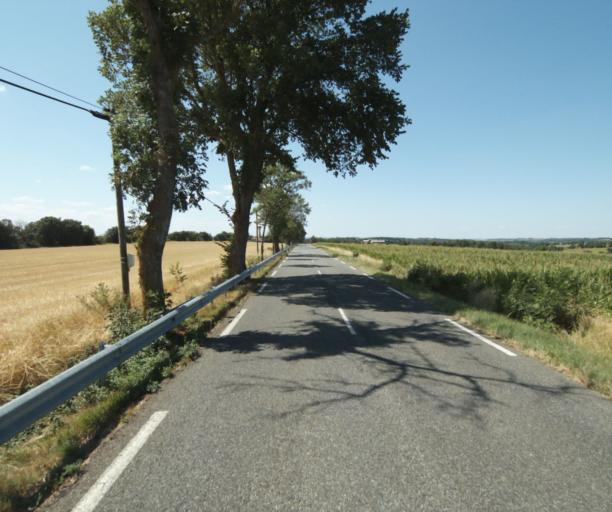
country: FR
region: Midi-Pyrenees
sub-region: Departement de la Haute-Garonne
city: Saint-Felix-Lauragais
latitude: 43.5022
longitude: 1.8771
